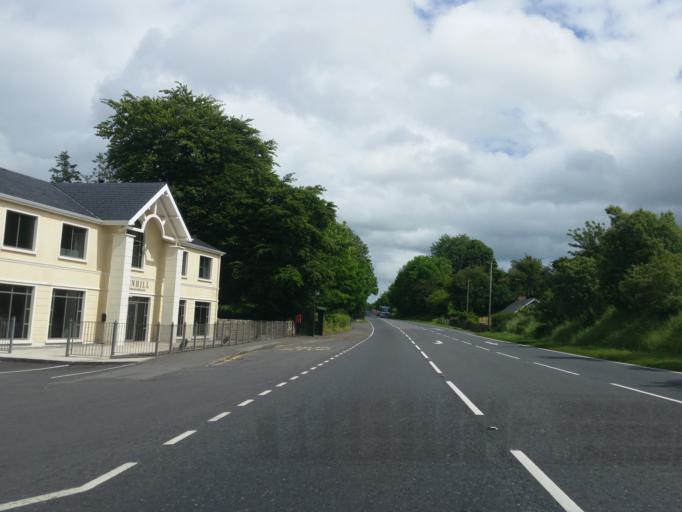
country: IE
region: Ulster
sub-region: County Monaghan
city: Monaghan
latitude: 54.4743
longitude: -7.0670
